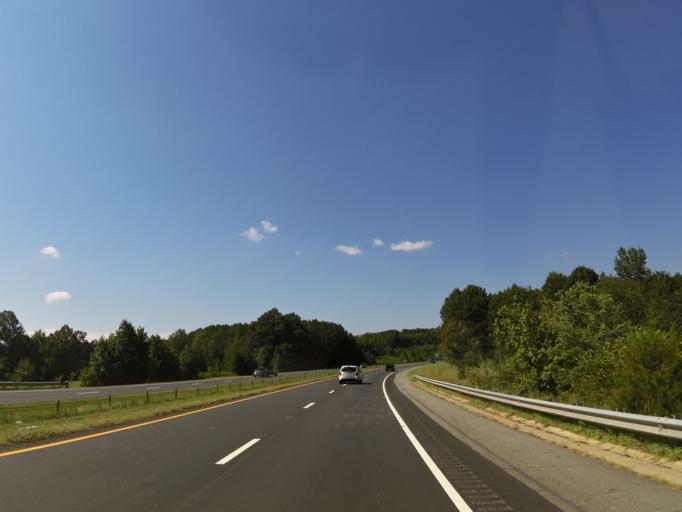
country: US
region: North Carolina
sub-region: Catawba County
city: Maiden
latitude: 35.5583
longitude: -81.2466
